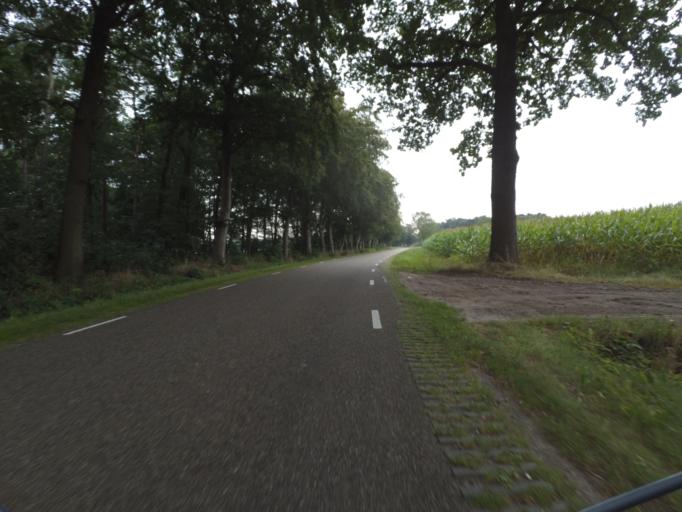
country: NL
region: Overijssel
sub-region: Gemeente Losser
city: Losser
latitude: 52.2959
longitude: 7.0182
